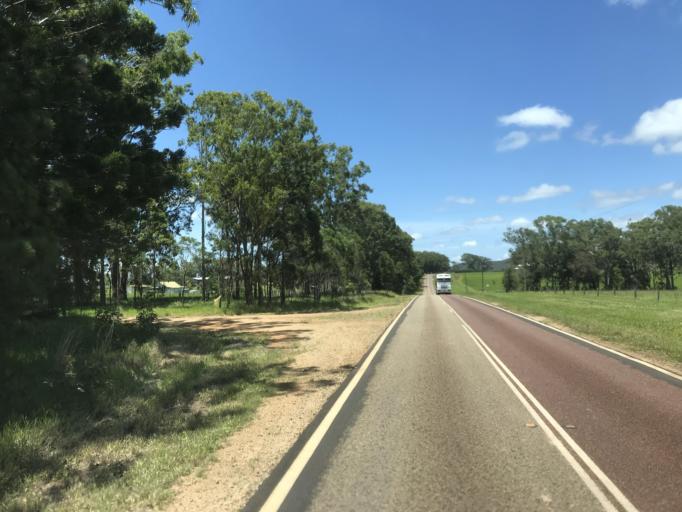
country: AU
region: Queensland
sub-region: Tablelands
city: Ravenshoe
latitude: -17.5196
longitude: 145.4517
